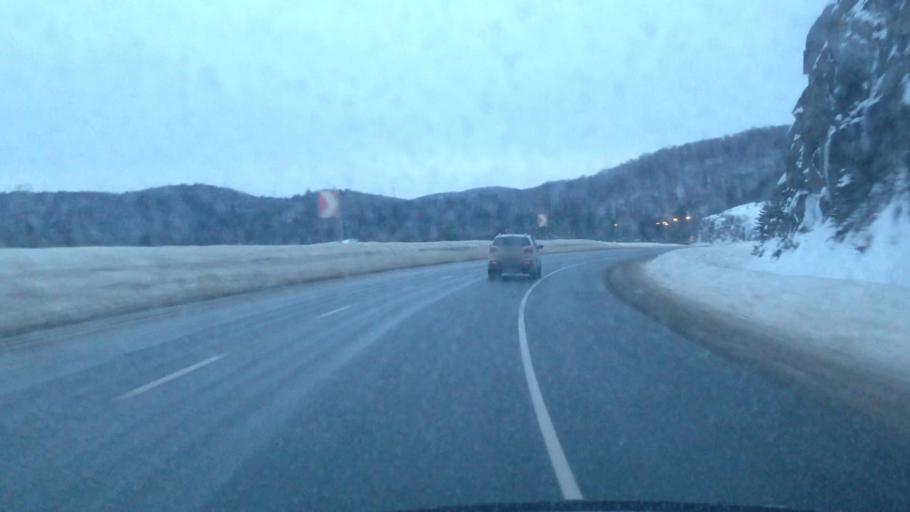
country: CA
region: Quebec
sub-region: Laurentides
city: Sainte-Agathe-des-Monts
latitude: 46.1094
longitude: -74.4187
